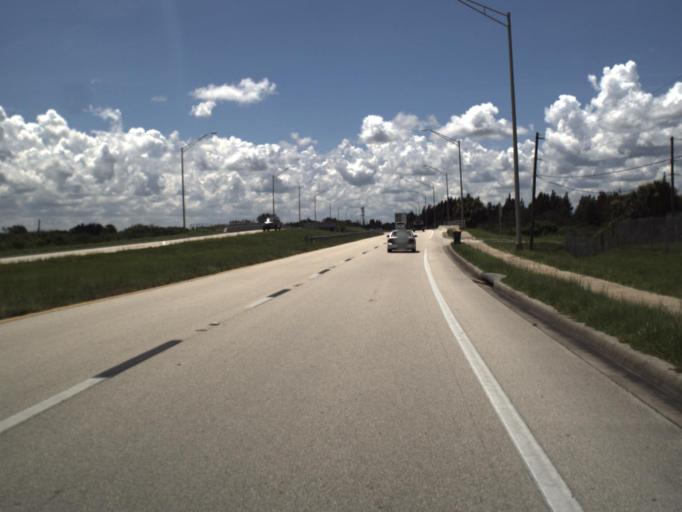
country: US
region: Florida
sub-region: Charlotte County
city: Cleveland
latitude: 26.9845
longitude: -81.9592
